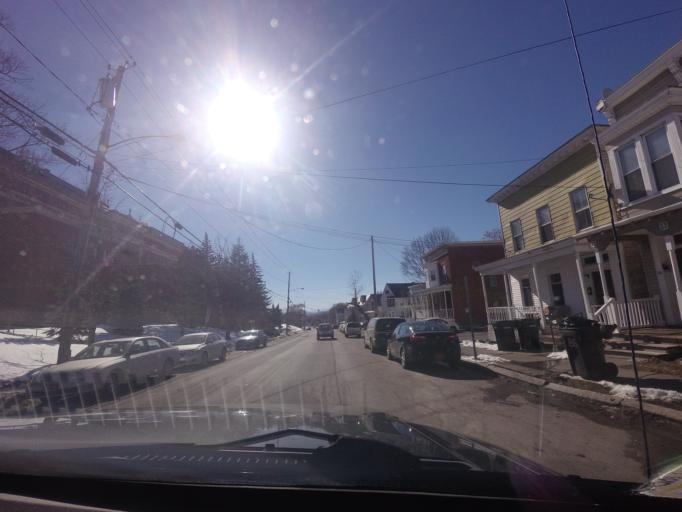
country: US
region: New York
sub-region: Albany County
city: Green Island
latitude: 42.7439
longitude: -73.6767
